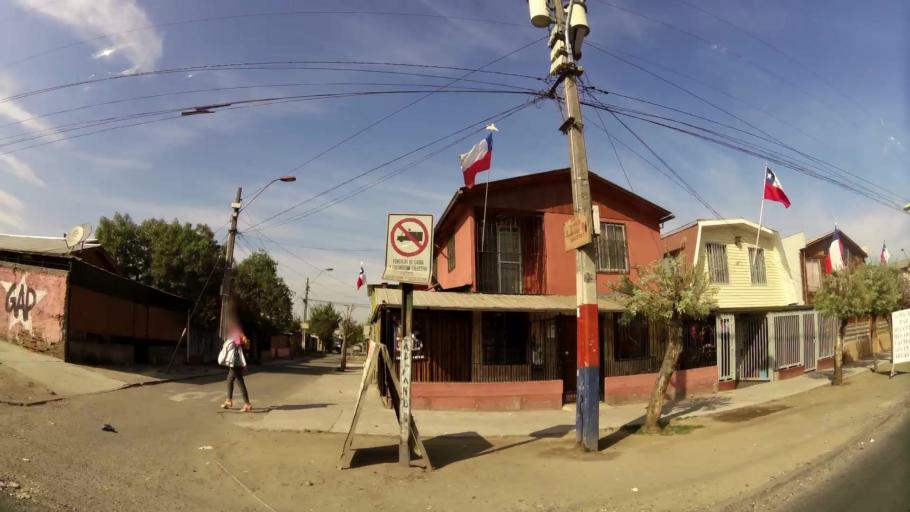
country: CL
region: Santiago Metropolitan
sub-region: Provincia de Santiago
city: La Pintana
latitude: -33.5540
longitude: -70.6337
